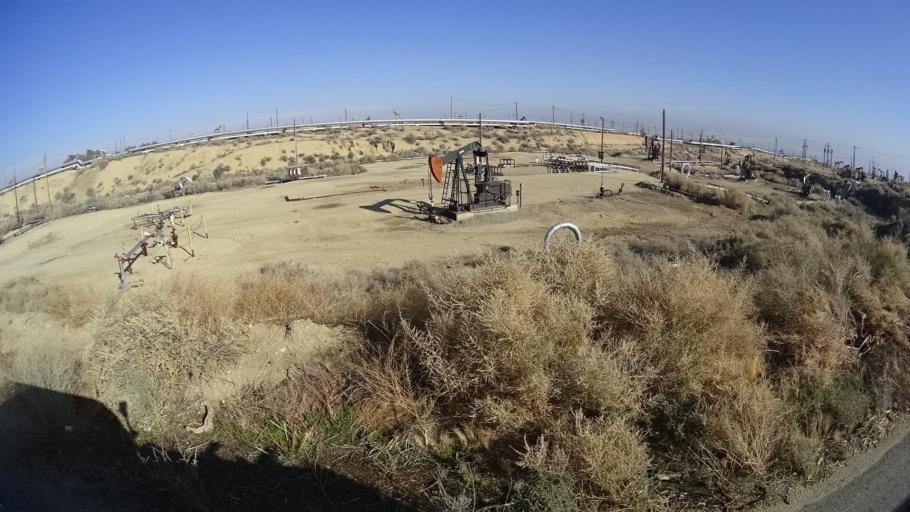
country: US
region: California
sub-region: Kern County
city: Taft Heights
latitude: 35.2234
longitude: -119.6212
